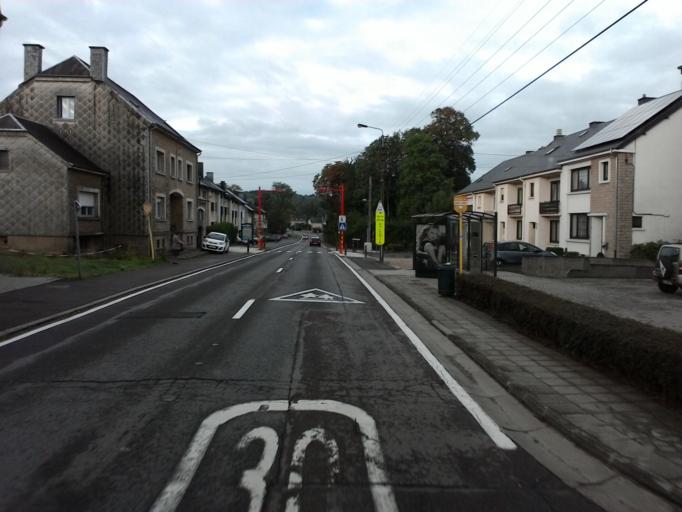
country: BE
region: Wallonia
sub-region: Province du Luxembourg
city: Arlon
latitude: 49.6774
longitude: 5.7969
